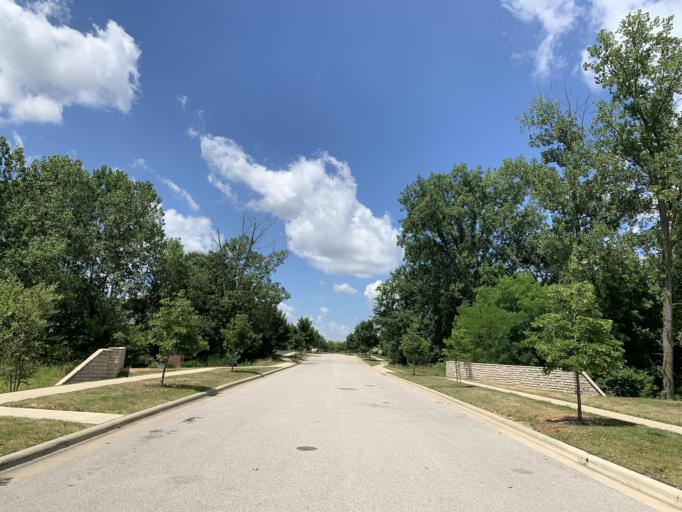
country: US
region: Ohio
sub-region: Union County
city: New California
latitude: 40.1414
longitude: -83.1724
